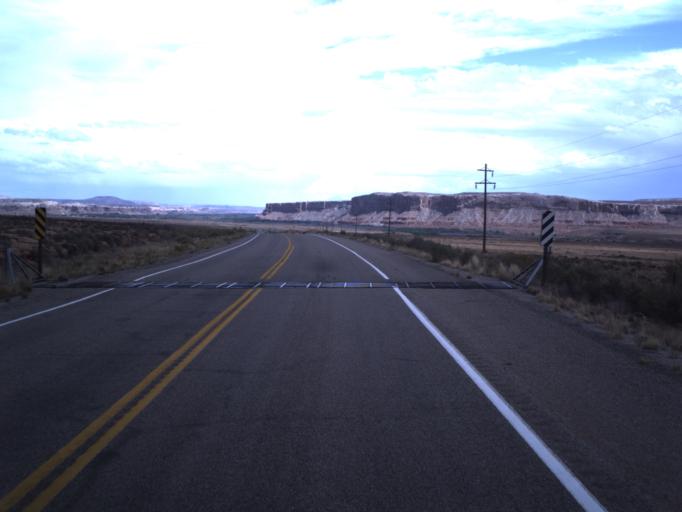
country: US
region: Utah
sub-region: San Juan County
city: Blanding
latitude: 37.2642
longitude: -109.6397
